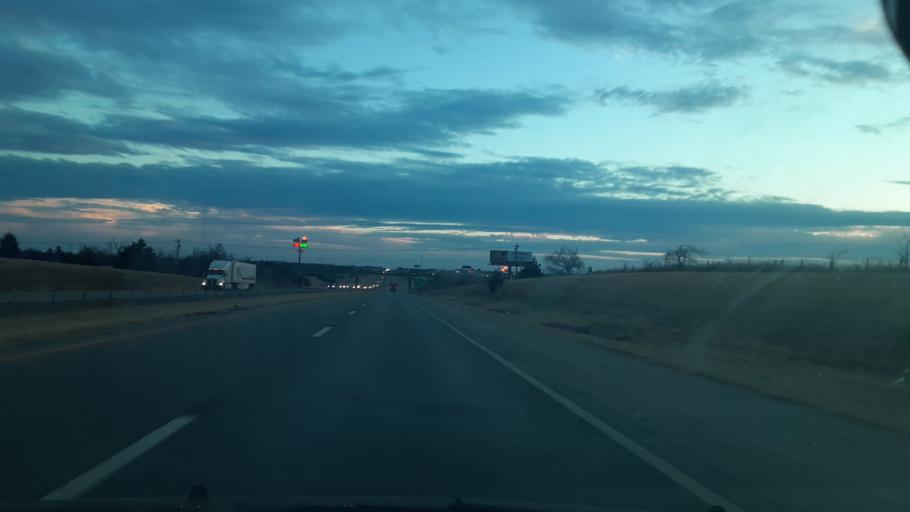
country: US
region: Oklahoma
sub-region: Logan County
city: Guthrie
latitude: 35.8875
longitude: -97.3942
